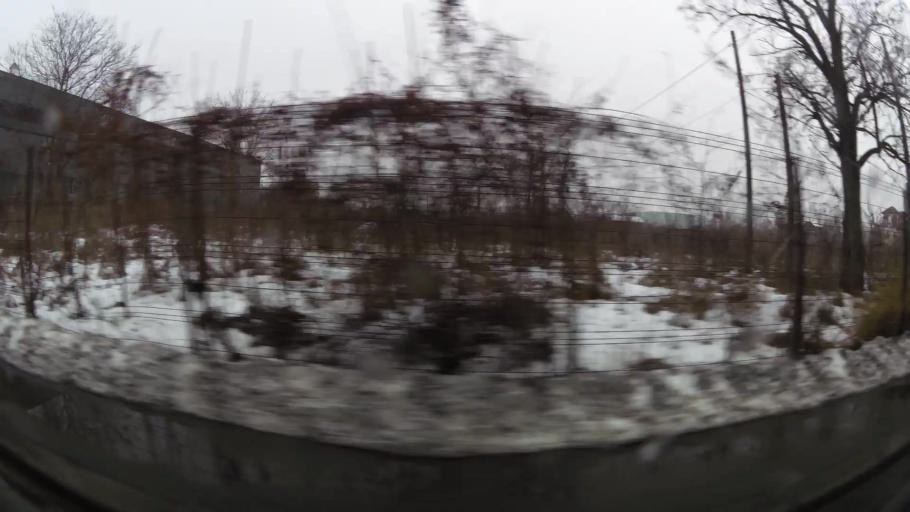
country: RO
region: Ilfov
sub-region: Comuna Otopeni
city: Otopeni
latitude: 44.4862
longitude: 26.0666
